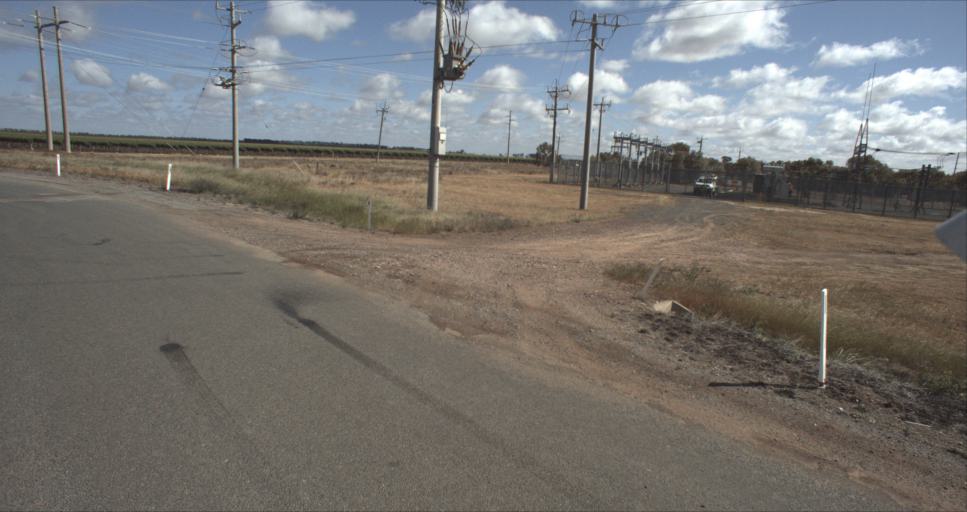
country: AU
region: New South Wales
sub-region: Murrumbidgee Shire
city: Darlington Point
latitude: -34.5137
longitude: 146.1777
